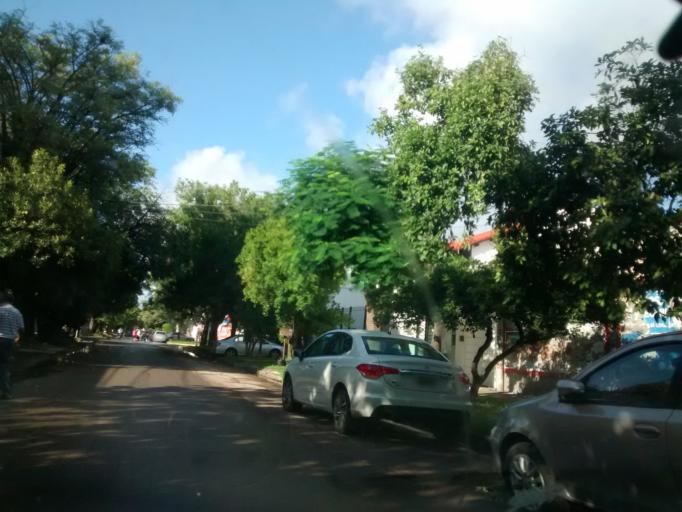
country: AR
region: Chaco
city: Resistencia
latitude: -27.4514
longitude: -58.9799
